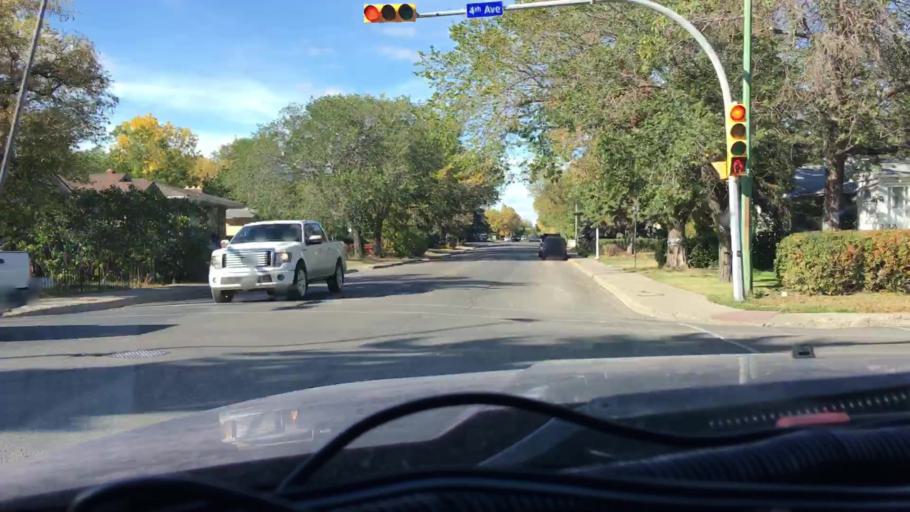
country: CA
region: Saskatchewan
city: Regina
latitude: 50.4628
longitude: -104.6311
